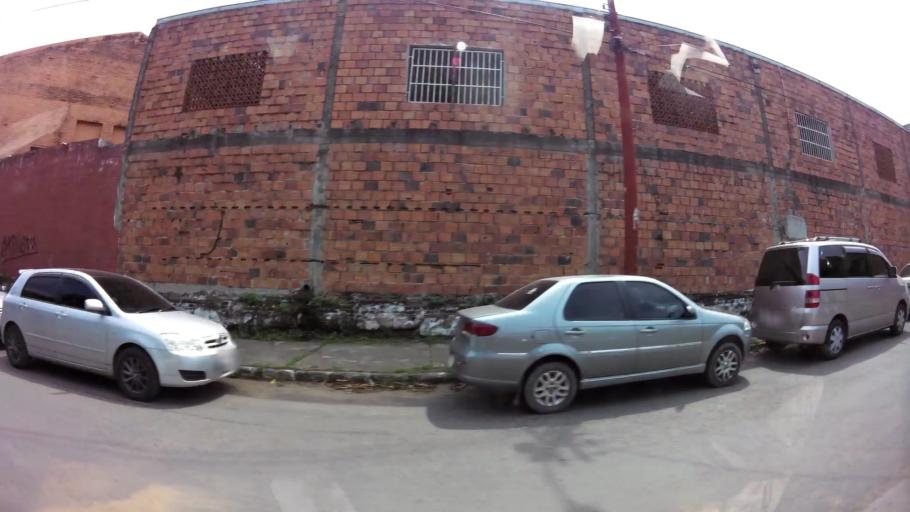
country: PY
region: Asuncion
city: Asuncion
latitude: -25.2682
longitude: -57.5835
